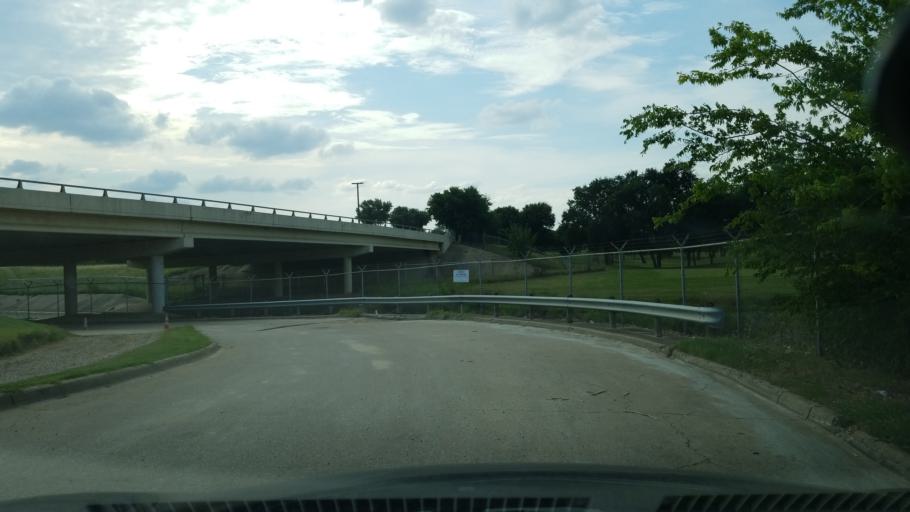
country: US
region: Texas
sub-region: Dallas County
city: Irving
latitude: 32.8725
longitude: -96.9585
